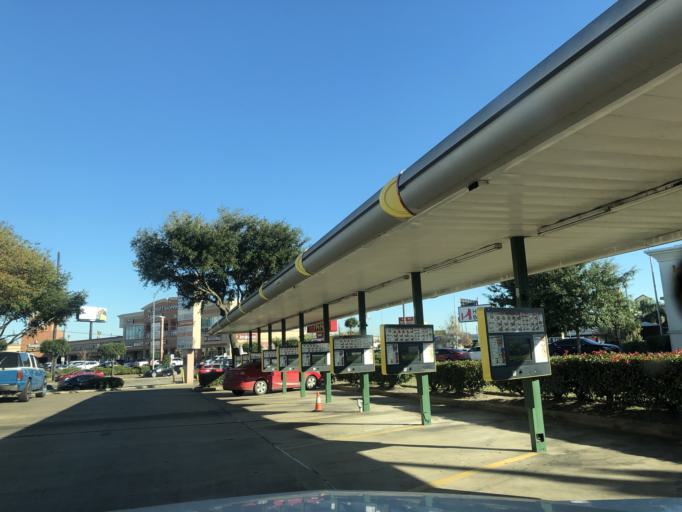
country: US
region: Texas
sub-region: Harris County
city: Bellaire
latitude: 29.7182
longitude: -95.5012
